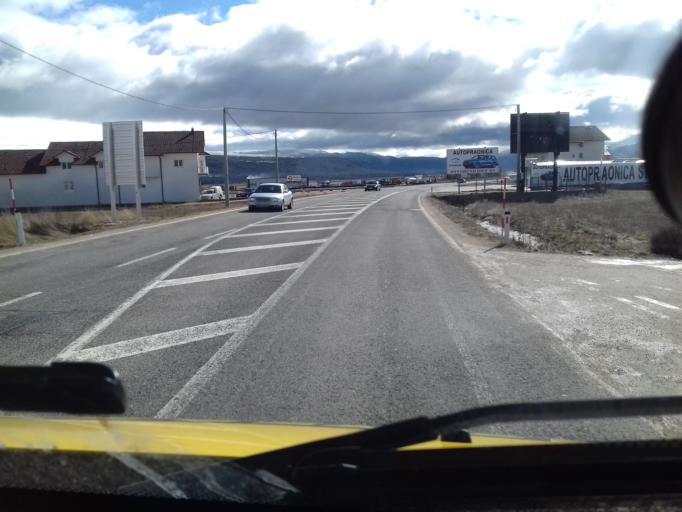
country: BA
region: Federation of Bosnia and Herzegovina
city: Tomislavgrad
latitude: 43.7183
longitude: 17.2357
